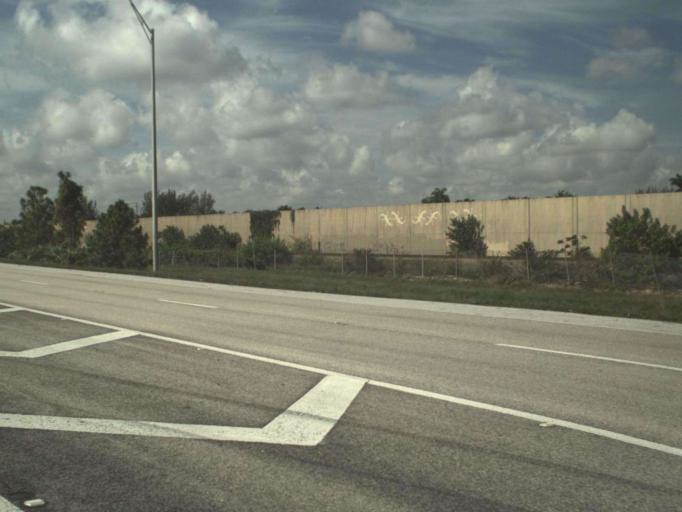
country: US
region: Florida
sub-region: Palm Beach County
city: Lake Clarke Shores
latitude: 26.6588
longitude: -80.0705
